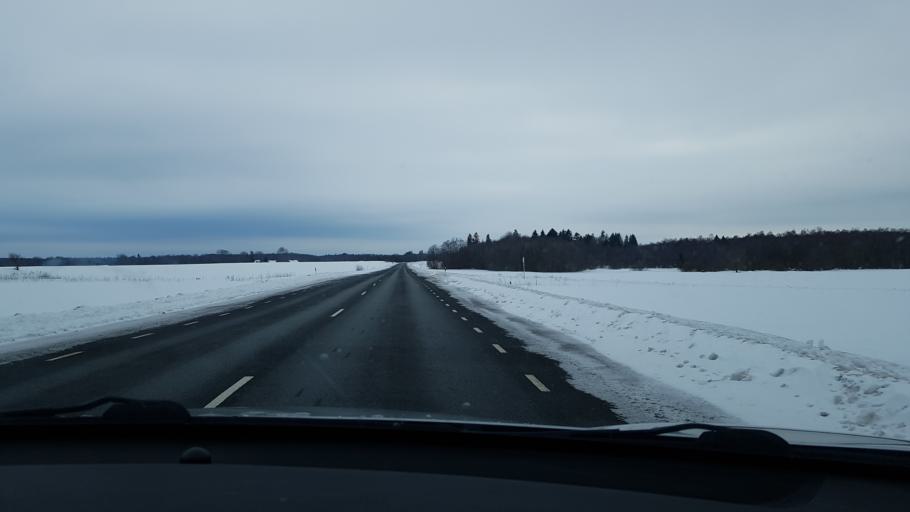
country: EE
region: Jaervamaa
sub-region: Jaerva-Jaani vald
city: Jarva-Jaani
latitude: 58.9024
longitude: 25.8077
